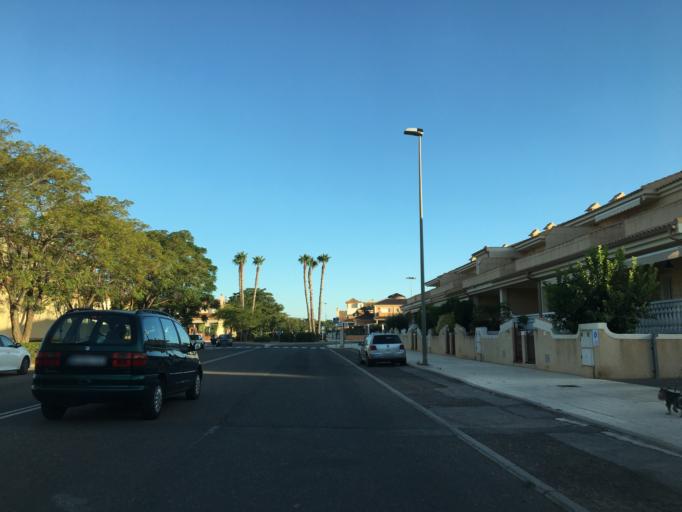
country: ES
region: Murcia
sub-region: Murcia
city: Cartagena
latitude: 37.6538
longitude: -1.0176
